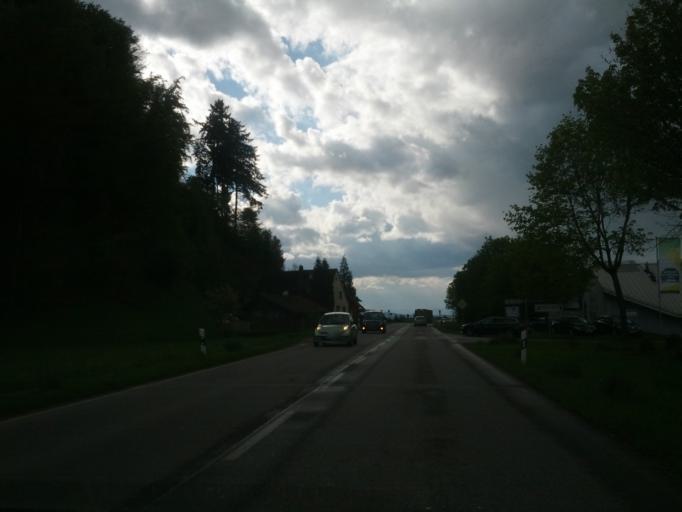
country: DE
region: Baden-Wuerttemberg
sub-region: Freiburg Region
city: Heuweiler
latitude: 48.0539
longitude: 7.9231
